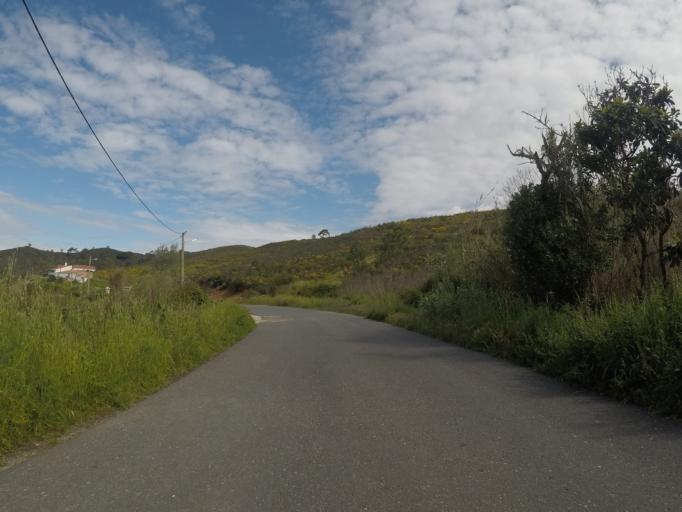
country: PT
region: Beja
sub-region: Odemira
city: Sao Teotonio
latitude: 37.4356
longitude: -8.7648
